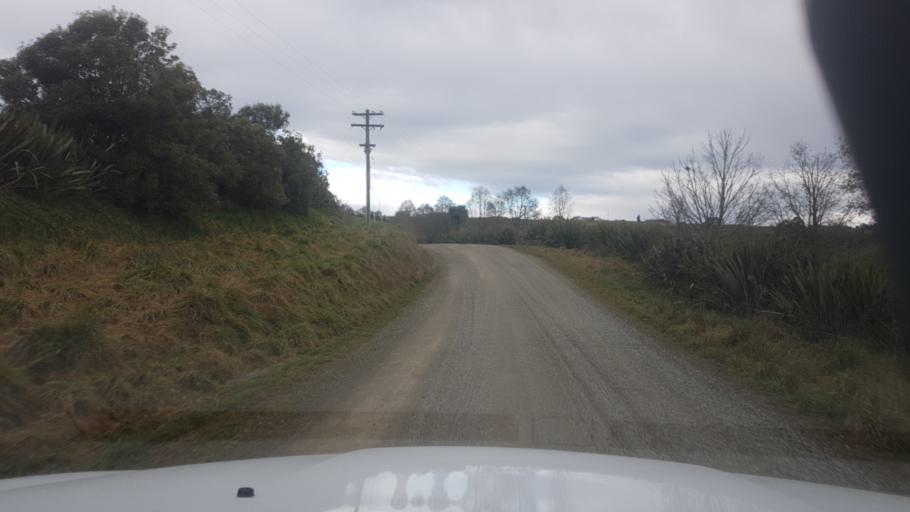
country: NZ
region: Canterbury
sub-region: Timaru District
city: Pleasant Point
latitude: -44.3478
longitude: 171.1567
